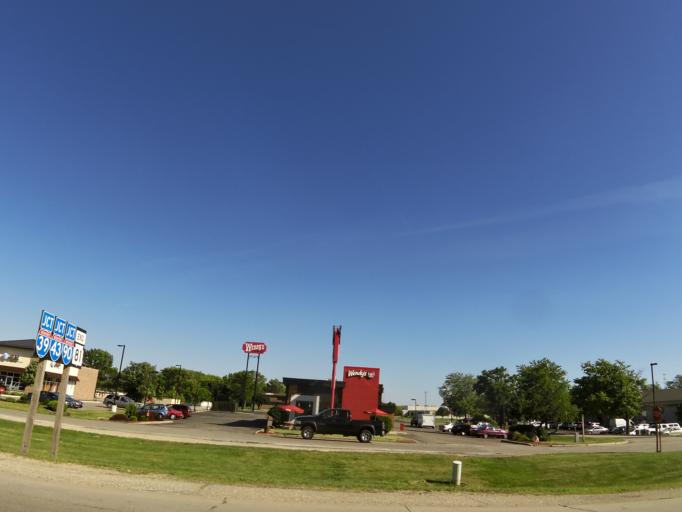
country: US
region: Wisconsin
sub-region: Rock County
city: Beloit
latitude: 42.5247
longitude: -88.9824
